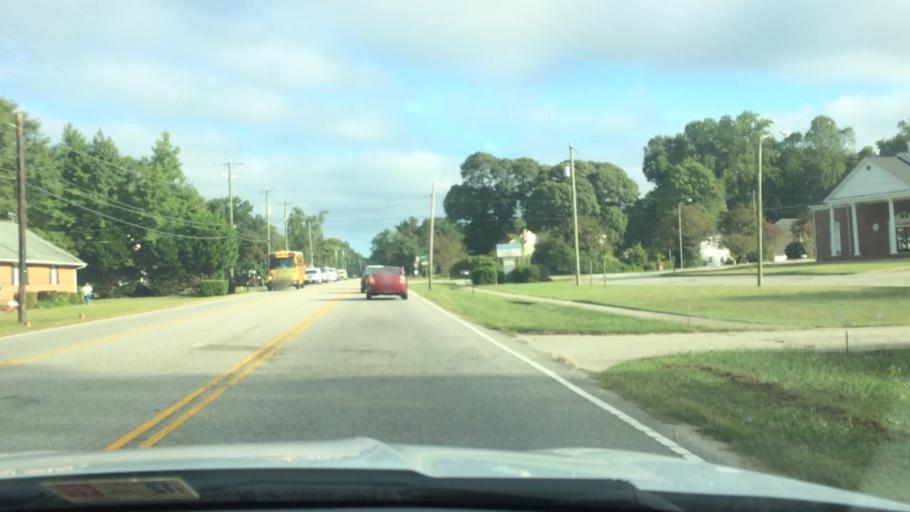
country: US
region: Virginia
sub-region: City of Williamsburg
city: Williamsburg
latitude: 37.2217
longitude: -76.6258
